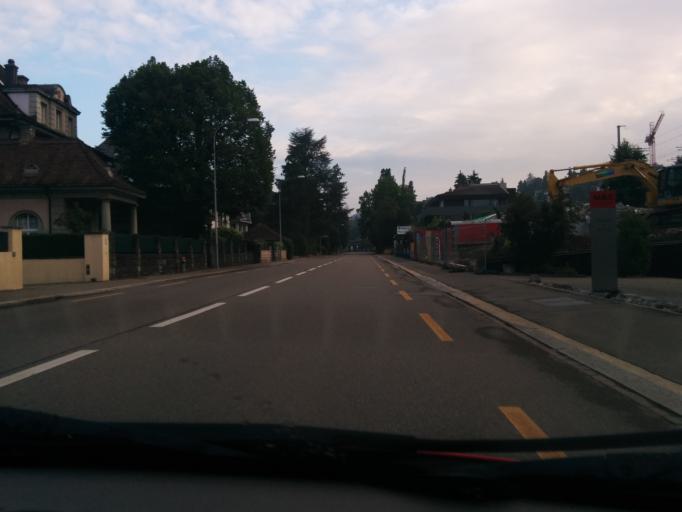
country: CH
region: Zurich
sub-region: Bezirk Meilen
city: Zollikon
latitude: 47.3400
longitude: 8.5677
